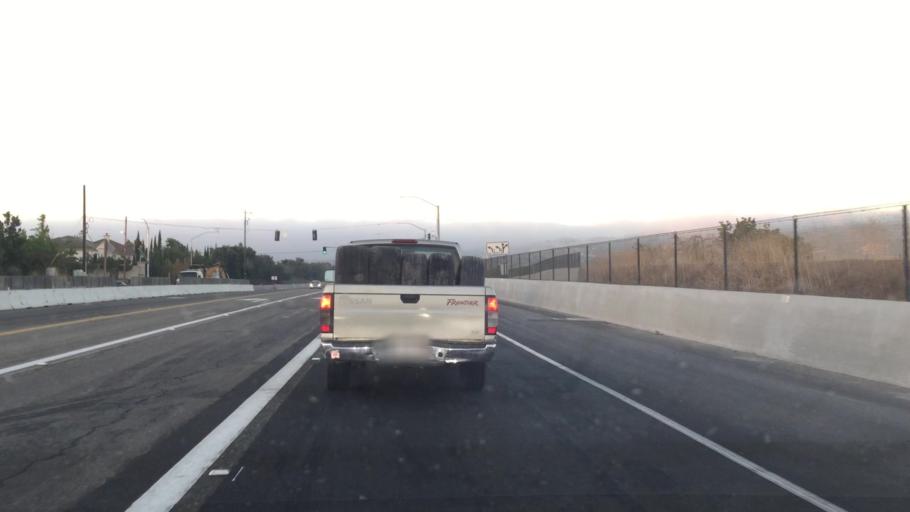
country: US
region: California
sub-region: Alameda County
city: Livermore
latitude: 37.6622
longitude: -121.8056
